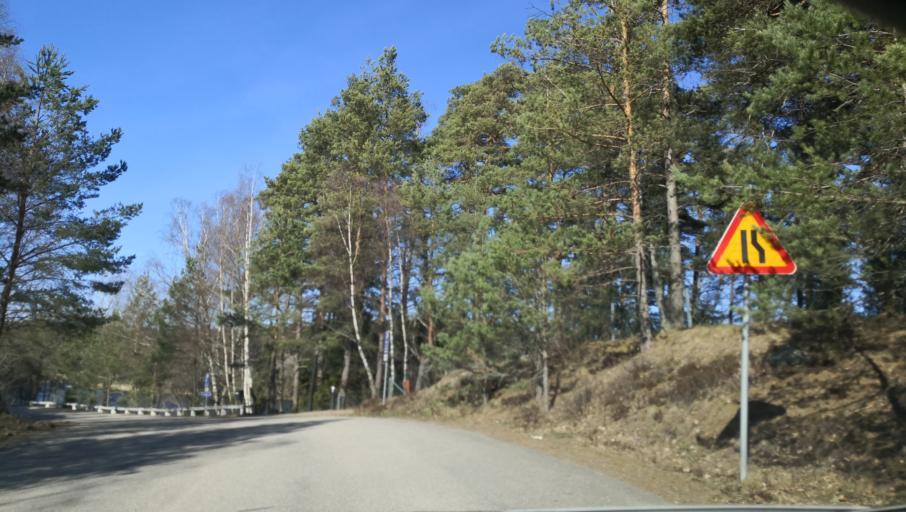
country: SE
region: Stockholm
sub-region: Varmdo Kommun
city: Mortnas
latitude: 59.2959
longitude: 18.4191
